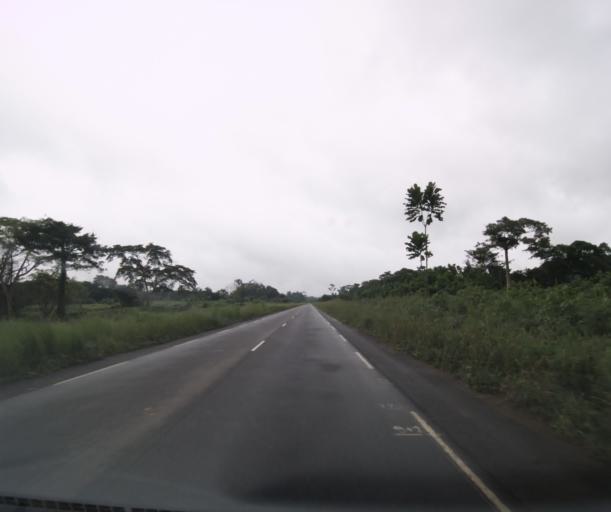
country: CM
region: Littoral
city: Edea
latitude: 3.4843
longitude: 10.1282
